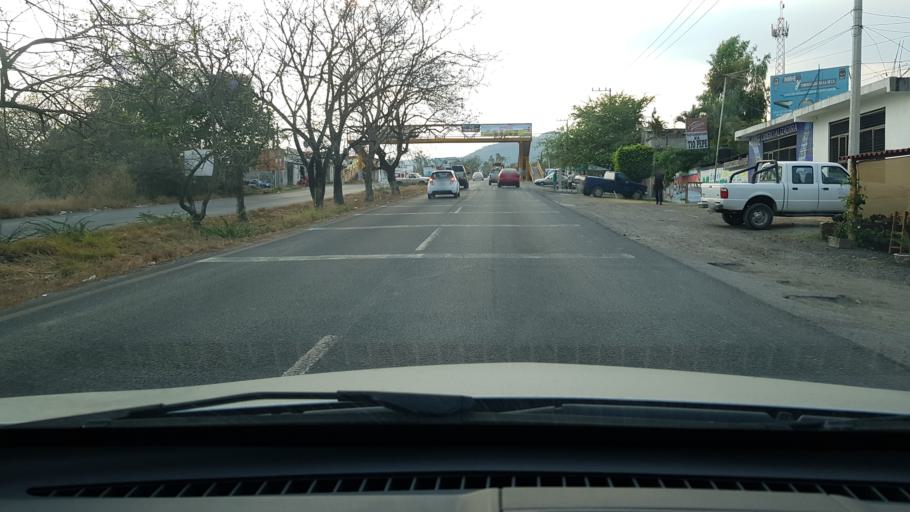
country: MX
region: Morelos
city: Yautepec
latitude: 18.8712
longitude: -99.0716
